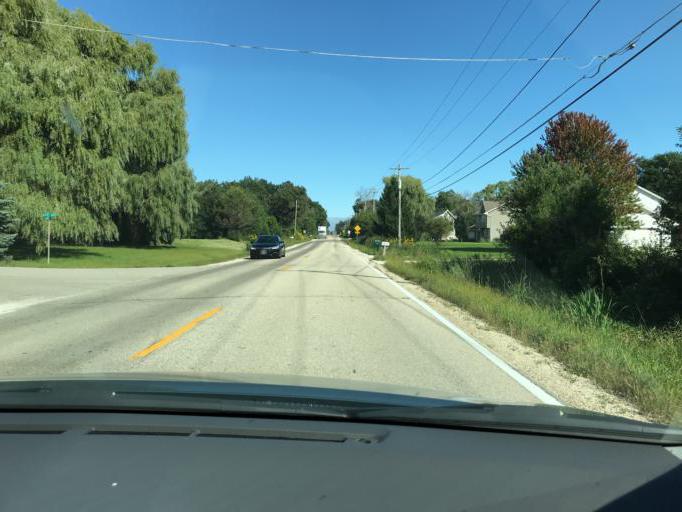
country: US
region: Illinois
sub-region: Lake County
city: Winthrop Harbor
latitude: 42.5224
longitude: -87.8483
